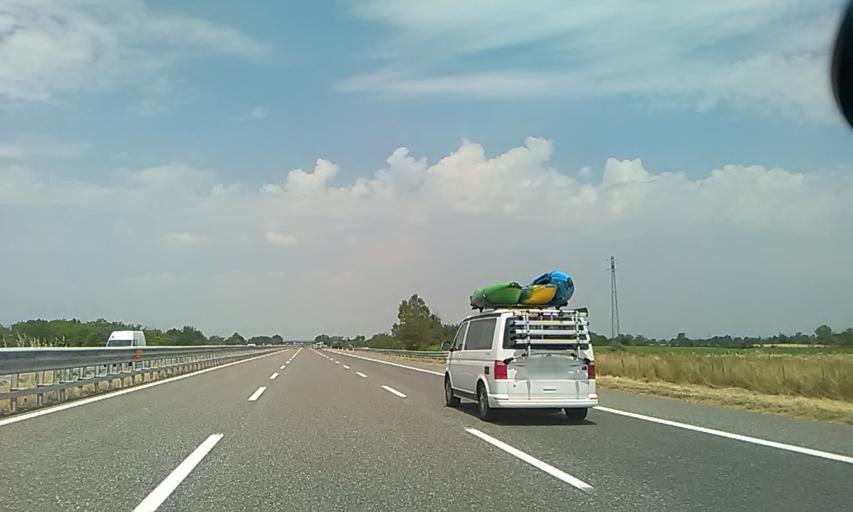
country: IT
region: Piedmont
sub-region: Provincia di Alessandria
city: Castelspina
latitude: 44.7972
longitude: 8.6090
